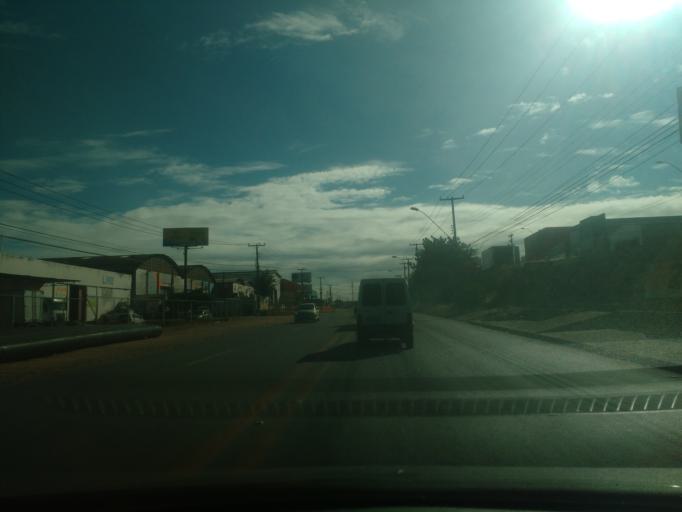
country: BR
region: Alagoas
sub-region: Satuba
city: Satuba
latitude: -9.5635
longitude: -35.7721
